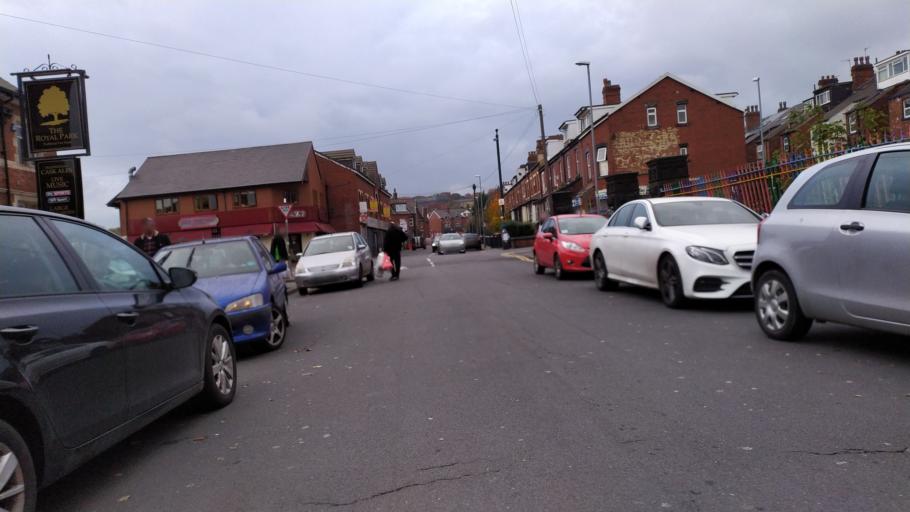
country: GB
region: England
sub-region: City and Borough of Leeds
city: Leeds
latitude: 53.8102
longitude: -1.5698
